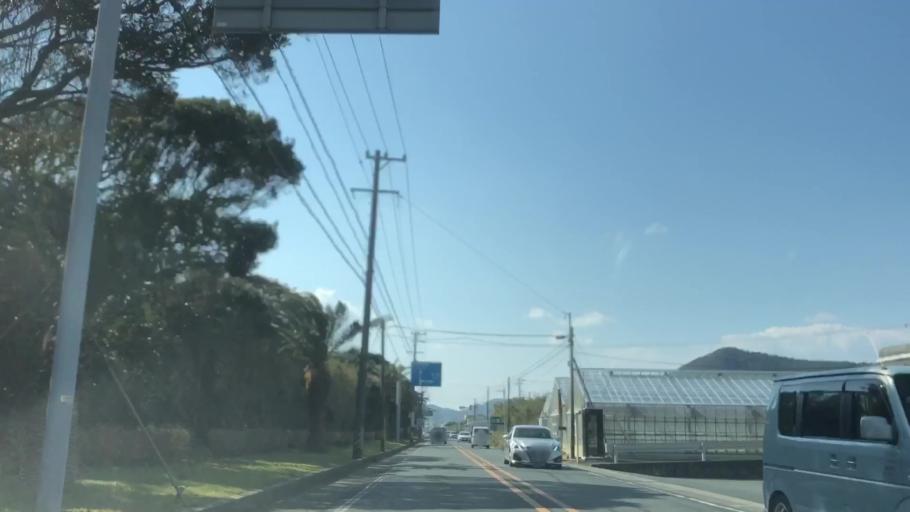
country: JP
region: Aichi
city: Toyohama
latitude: 34.5888
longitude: 137.0776
